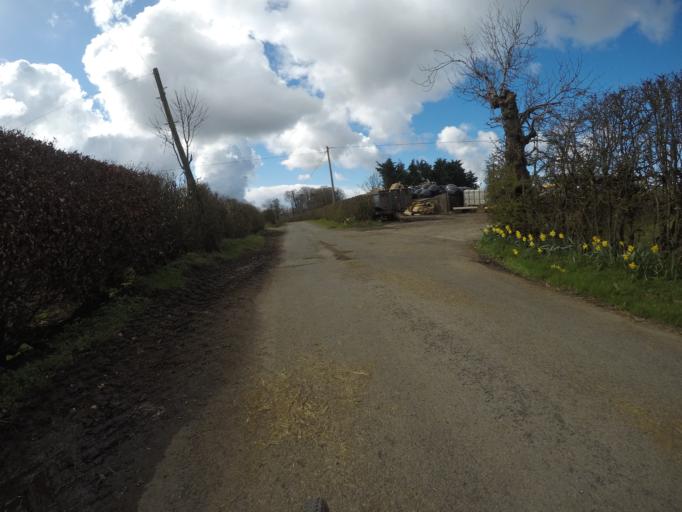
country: GB
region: Scotland
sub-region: North Ayrshire
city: Kilbirnie
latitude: 55.7226
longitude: -4.6666
